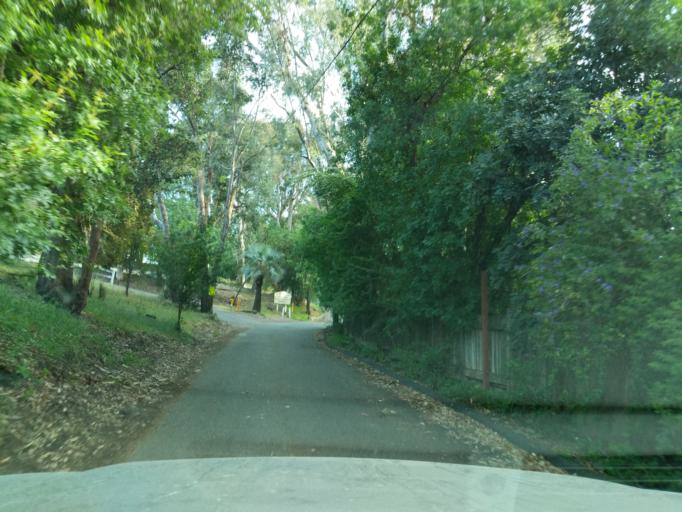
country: US
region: California
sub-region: Santa Clara County
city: Morgan Hill
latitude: 37.1218
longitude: -121.6602
